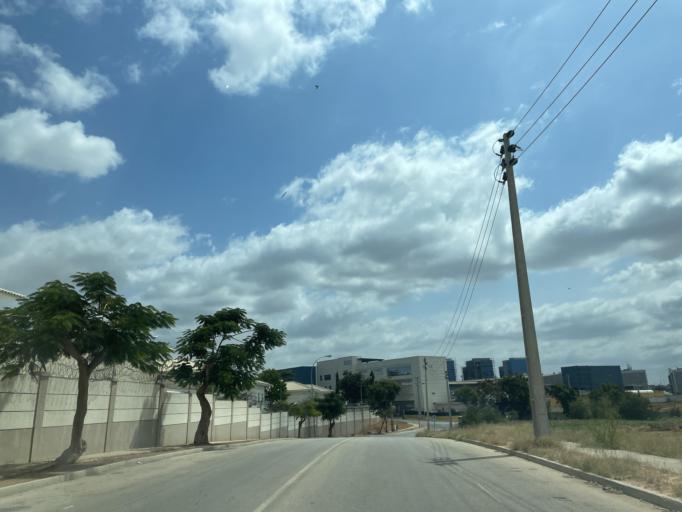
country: AO
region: Luanda
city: Luanda
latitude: -8.9308
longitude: 13.1856
